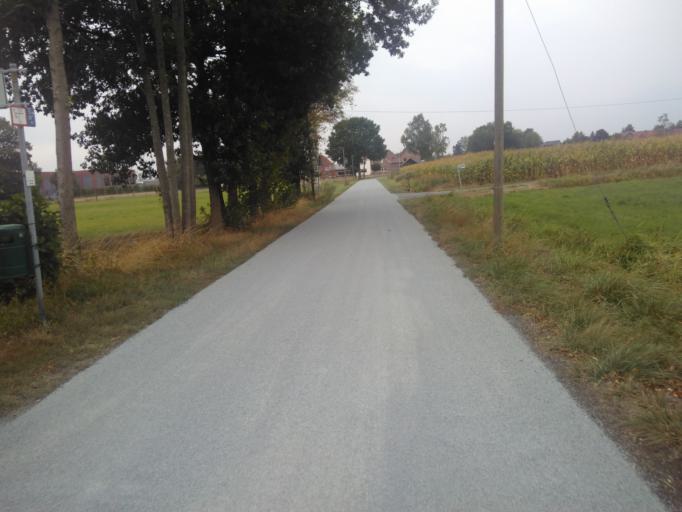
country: DE
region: North Rhine-Westphalia
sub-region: Regierungsbezirk Detmold
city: Verl
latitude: 51.8659
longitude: 8.4773
